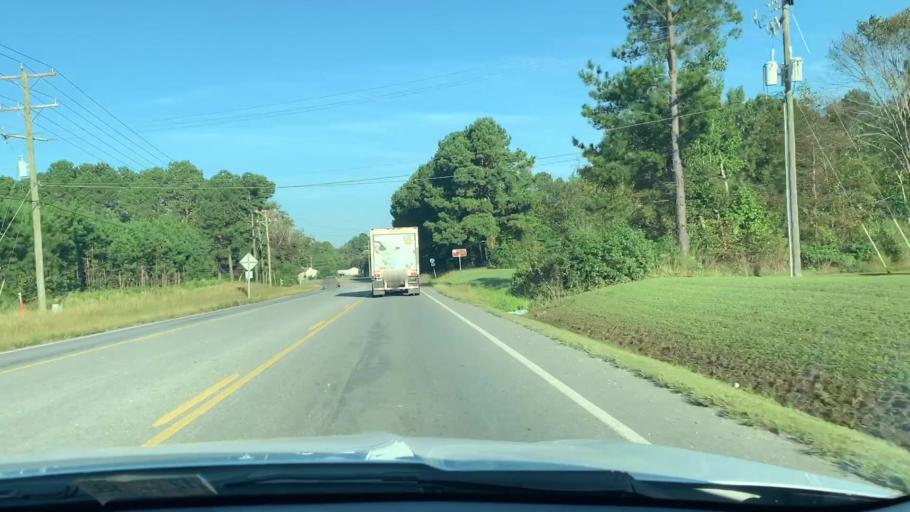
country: US
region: Virginia
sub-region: Middlesex County
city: Deltaville
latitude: 37.5533
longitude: -76.4492
